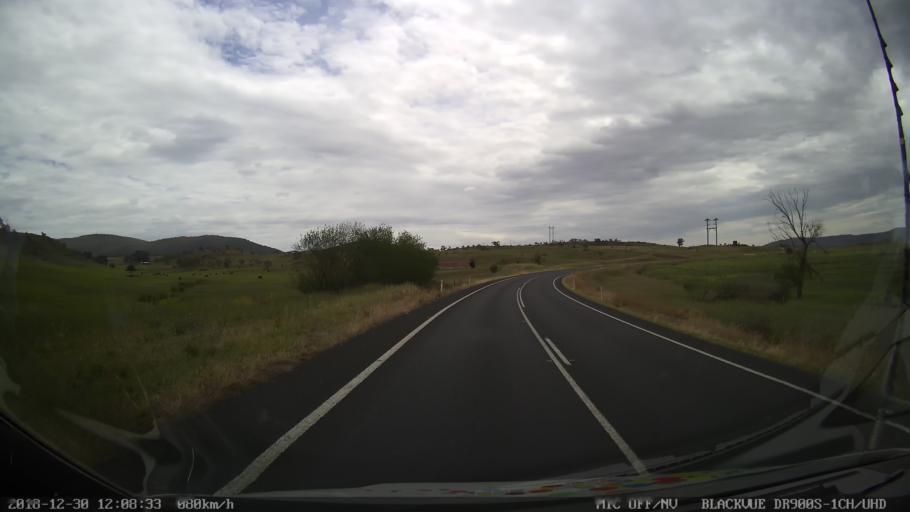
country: AU
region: New South Wales
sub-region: Snowy River
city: Jindabyne
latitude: -36.3938
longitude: 148.5941
